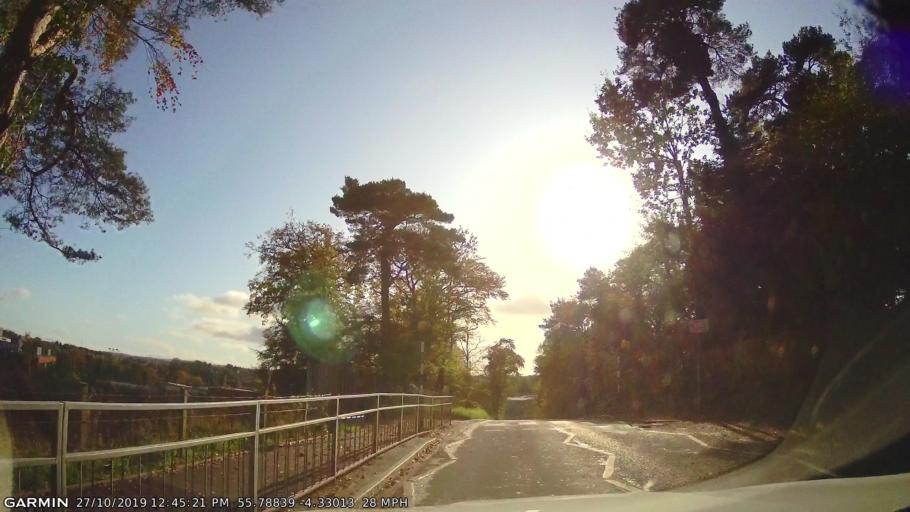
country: GB
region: Scotland
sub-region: East Renfrewshire
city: Newton Mearns
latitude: 55.7884
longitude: -4.3301
